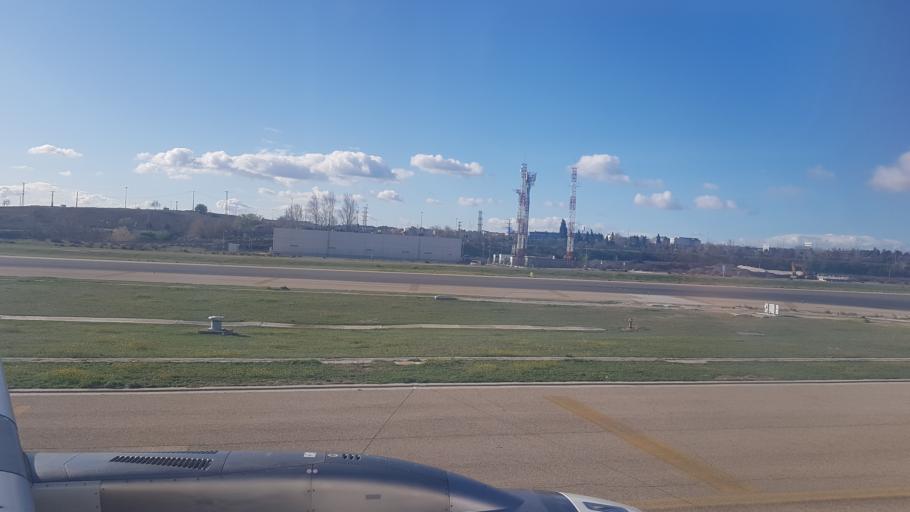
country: ES
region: Madrid
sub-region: Provincia de Madrid
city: Barajas de Madrid
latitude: 40.4858
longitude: -3.5855
